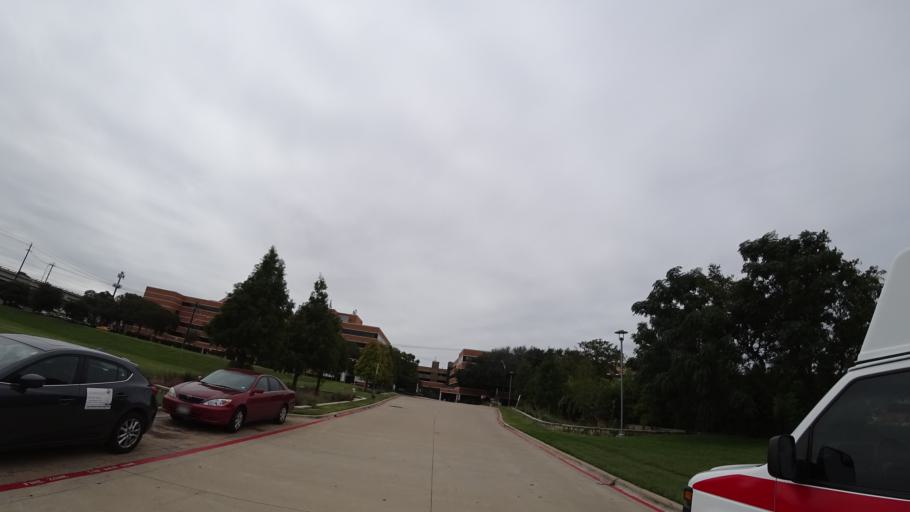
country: US
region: Texas
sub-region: Travis County
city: Austin
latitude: 30.2905
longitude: -97.7241
